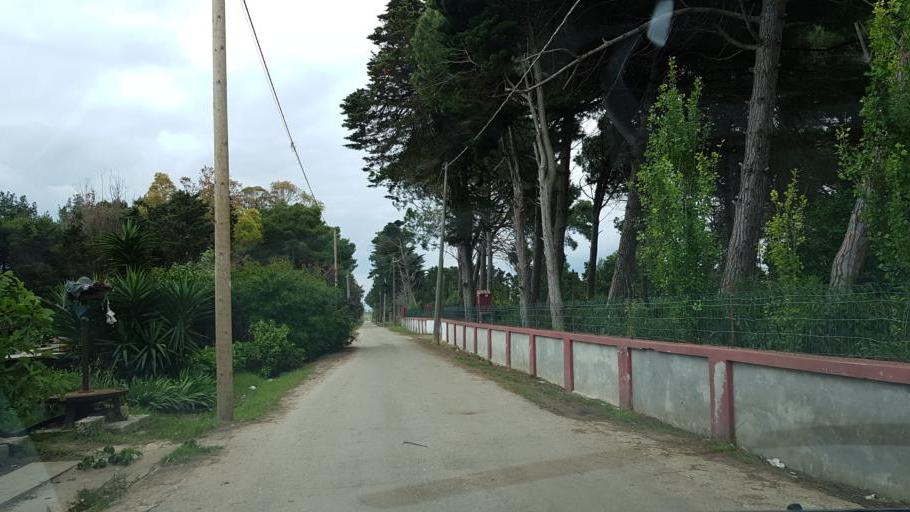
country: IT
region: Apulia
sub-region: Provincia di Brindisi
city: Brindisi
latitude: 40.6372
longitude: 17.8964
